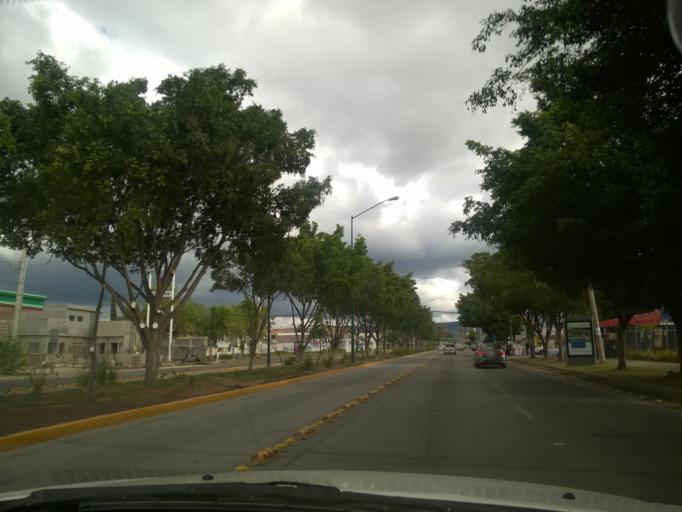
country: MX
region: Guanajuato
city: Leon
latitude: 21.1260
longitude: -101.6476
